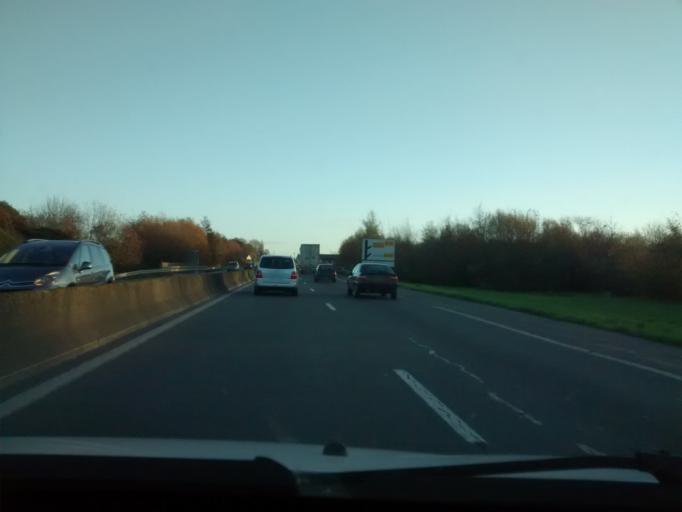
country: FR
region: Brittany
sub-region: Departement d'Ille-et-Vilaine
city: Saint-Jouan-des-Guerets
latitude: 48.6163
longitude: -1.9849
